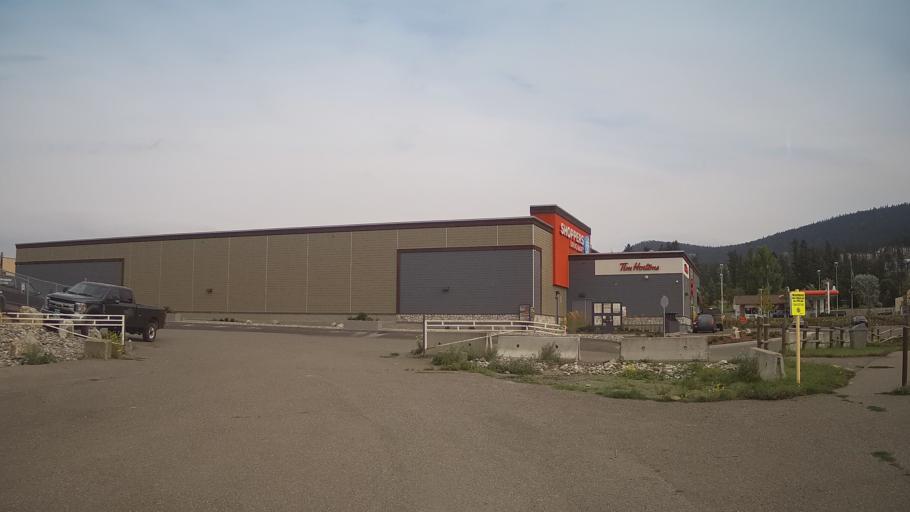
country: CA
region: British Columbia
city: Williams Lake
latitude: 52.1272
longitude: -122.1345
